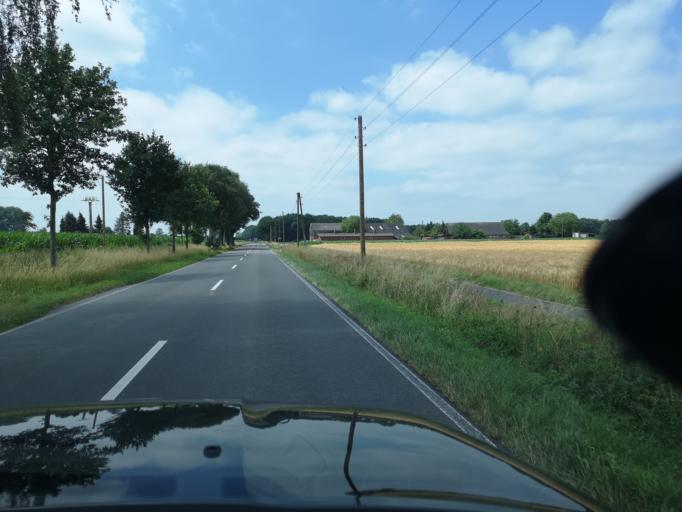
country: NL
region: Gelderland
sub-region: Gemeente Aalten
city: Aalten
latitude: 51.8789
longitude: 6.5761
